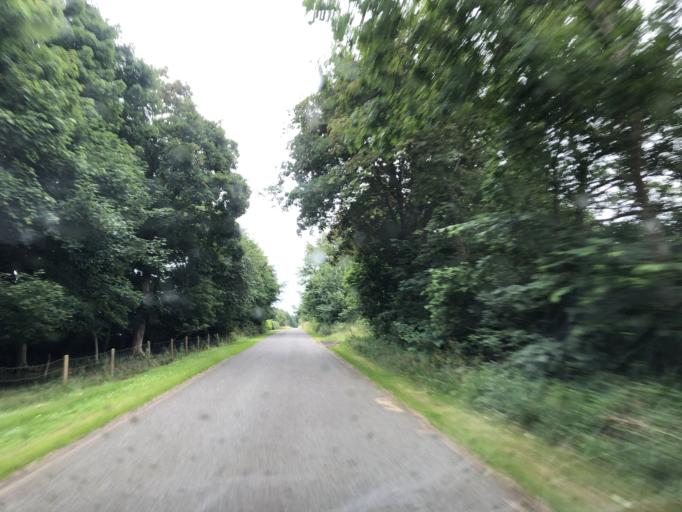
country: DK
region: Central Jutland
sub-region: Herning Kommune
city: Vildbjerg
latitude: 56.1983
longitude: 8.8441
